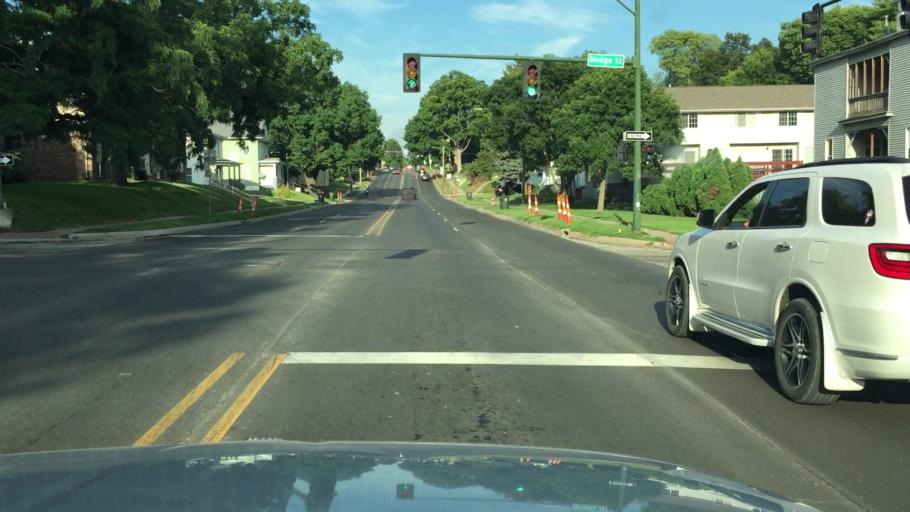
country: US
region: Iowa
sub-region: Johnson County
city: Iowa City
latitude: 41.6578
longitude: -91.5260
